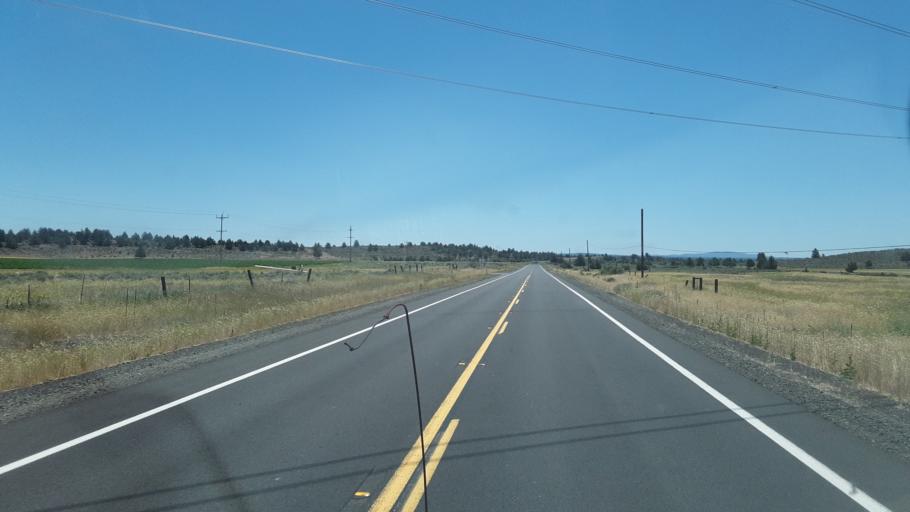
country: US
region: California
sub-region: Siskiyou County
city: Tulelake
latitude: 41.7188
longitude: -121.2917
